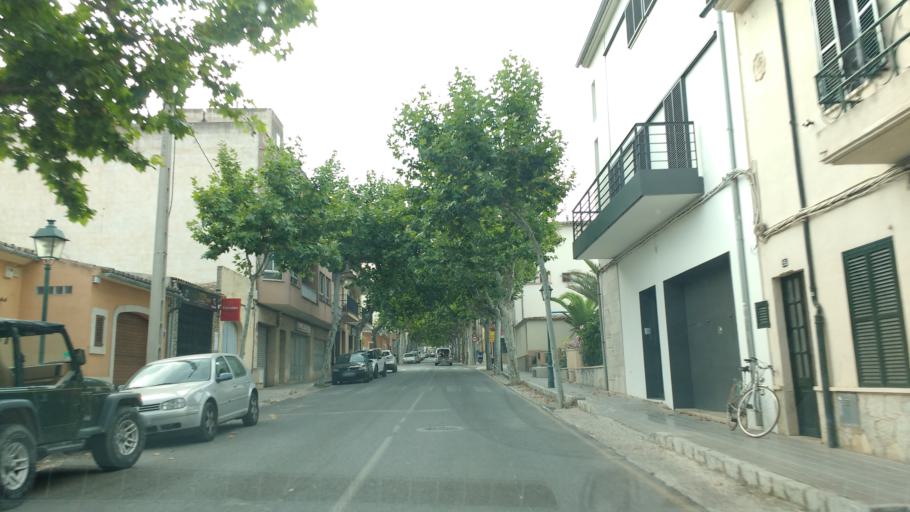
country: ES
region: Balearic Islands
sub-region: Illes Balears
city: Alaro
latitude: 39.7033
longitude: 2.7933
